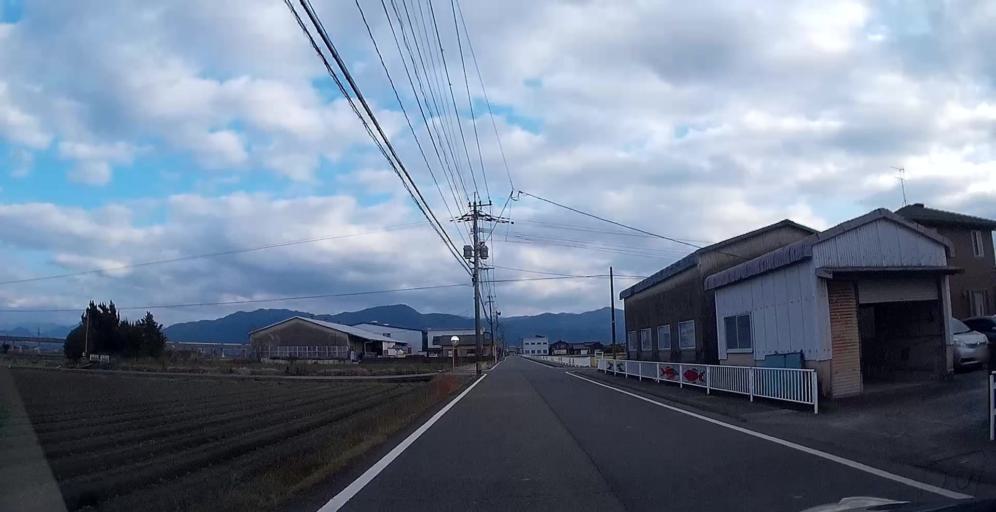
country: JP
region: Kumamoto
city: Yatsushiro
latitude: 32.5451
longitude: 130.6193
